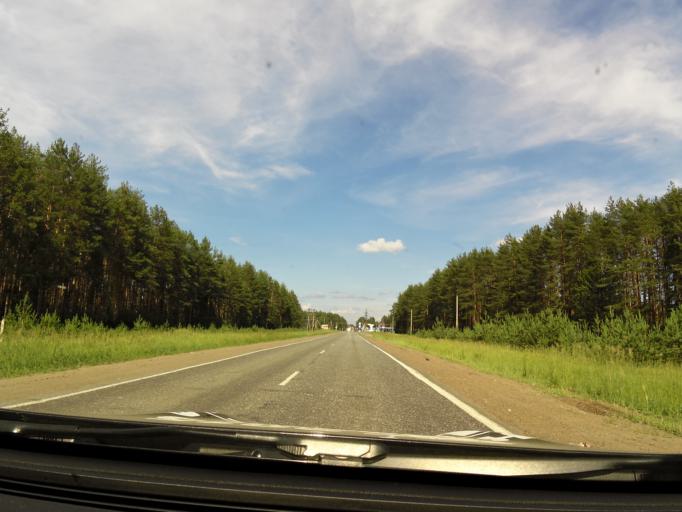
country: RU
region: Kirov
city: Belaya Kholunitsa
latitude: 58.8438
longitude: 50.8093
